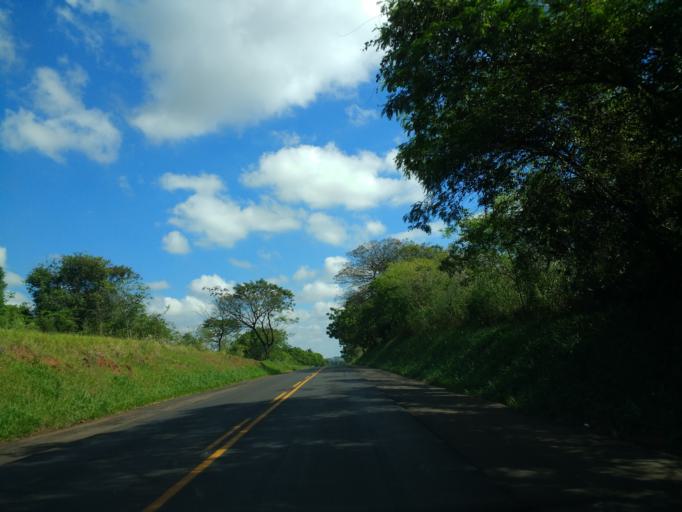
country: BR
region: Parana
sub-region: Umuarama
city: Umuarama
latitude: -23.8618
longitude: -53.3847
